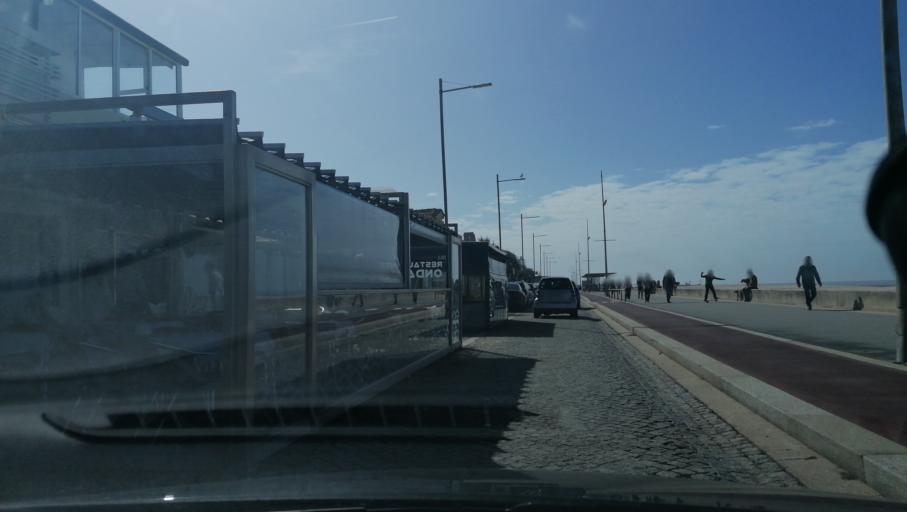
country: PT
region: Aveiro
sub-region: Espinho
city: Espinho
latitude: 41.0025
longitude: -8.6461
